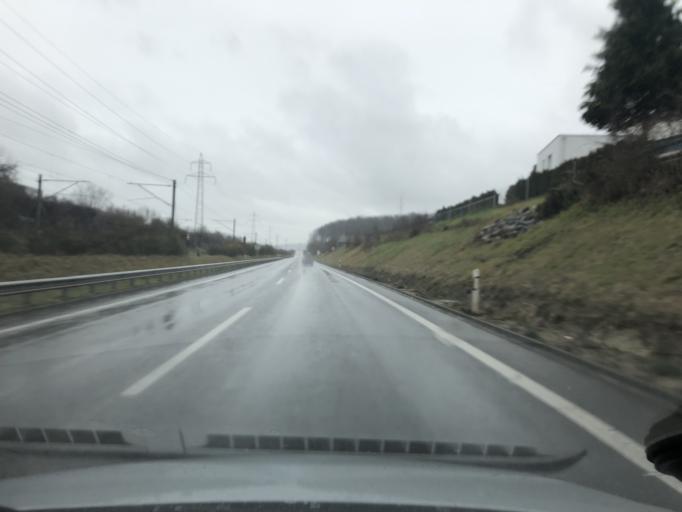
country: CH
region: Aargau
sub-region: Bezirk Brugg
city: Hausen
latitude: 47.4607
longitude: 8.2087
